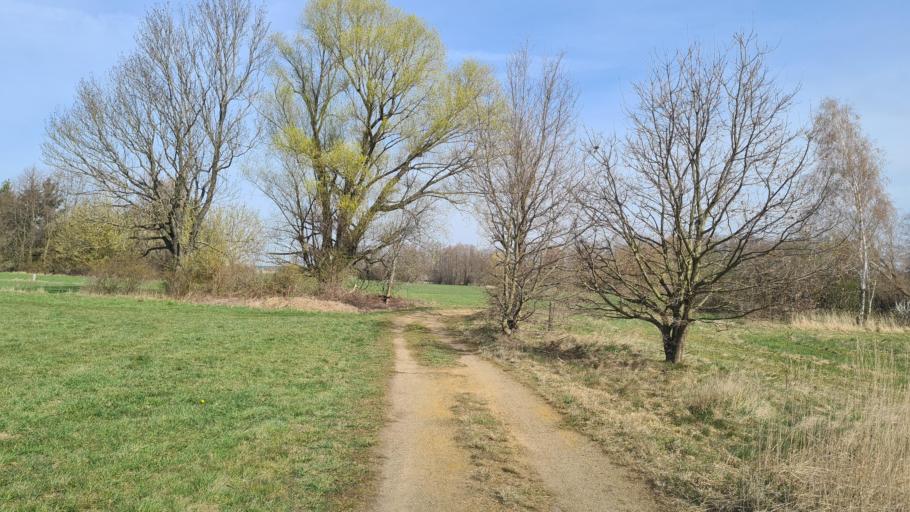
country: DE
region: Brandenburg
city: Sonnewalde
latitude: 51.7140
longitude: 13.6457
